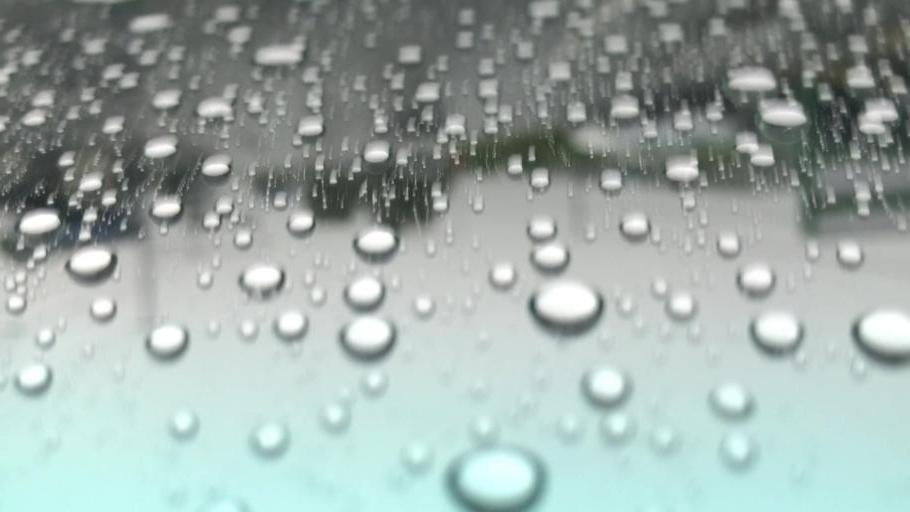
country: JP
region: Hokkaido
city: Nayoro
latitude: 44.2879
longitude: 142.4161
